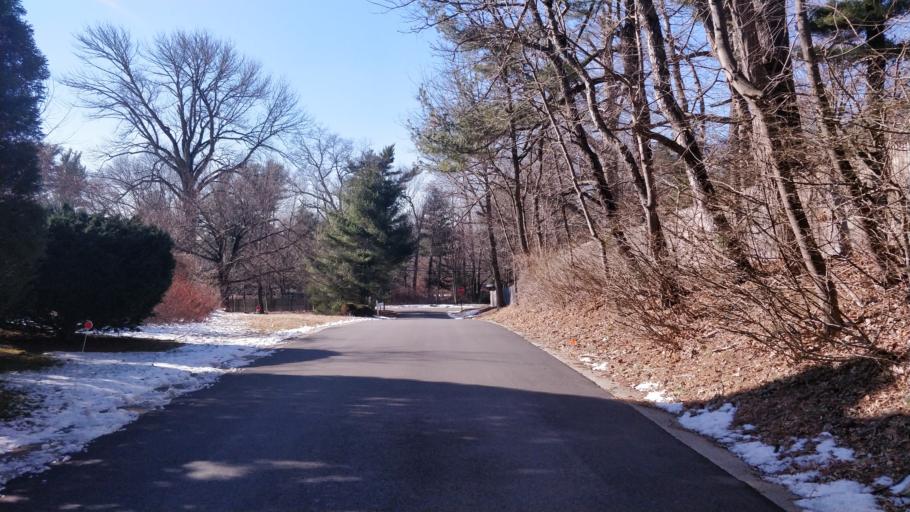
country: US
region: New York
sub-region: Nassau County
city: Westbury
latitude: 40.7753
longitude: -73.5847
